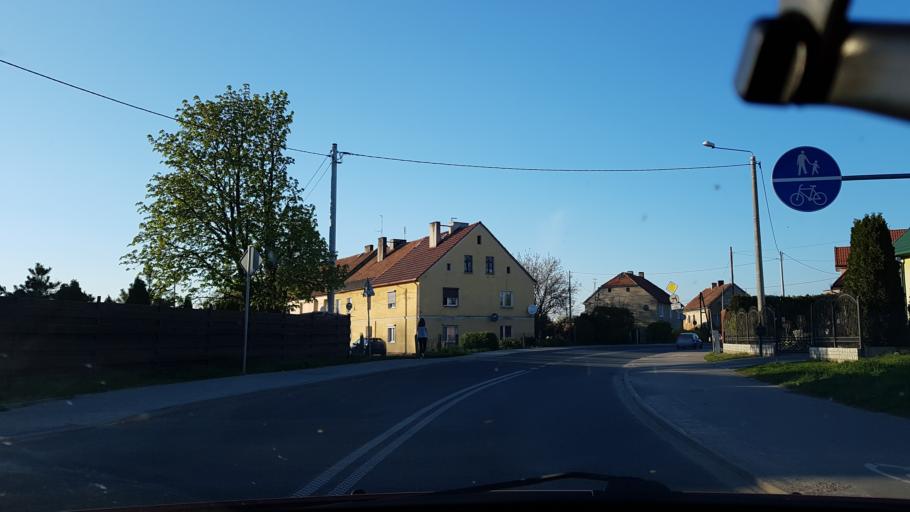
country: PL
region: Opole Voivodeship
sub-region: Powiat nyski
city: Nysa
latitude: 50.4348
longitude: 17.3054
